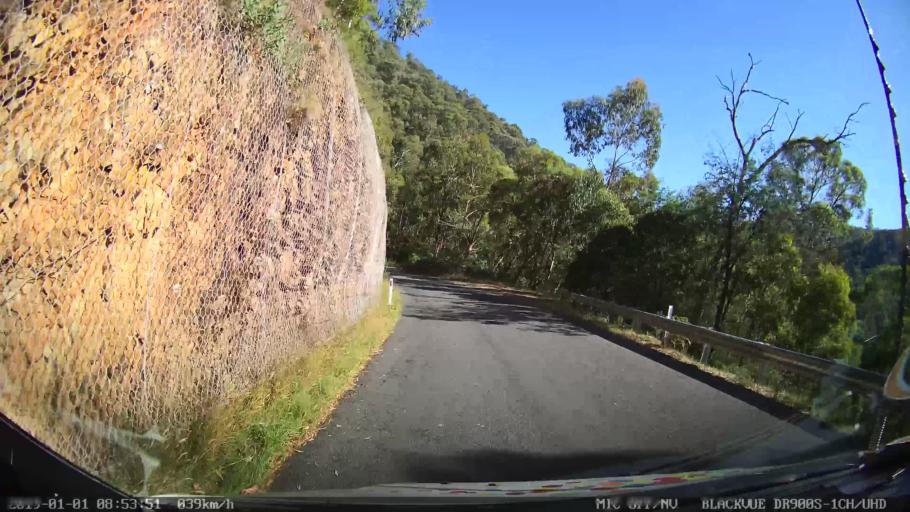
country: AU
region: New South Wales
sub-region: Snowy River
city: Jindabyne
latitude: -36.2632
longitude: 148.1900
